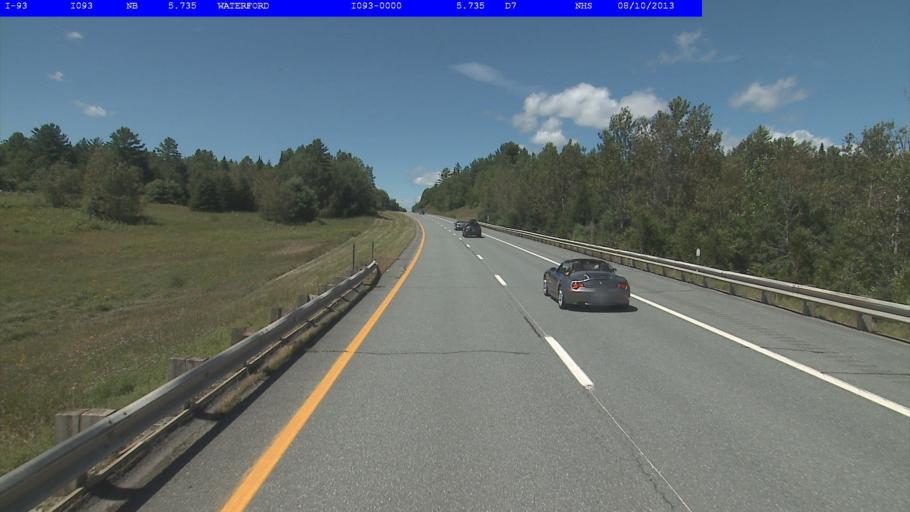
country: US
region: Vermont
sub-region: Caledonia County
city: Saint Johnsbury
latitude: 44.4166
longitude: -71.9261
